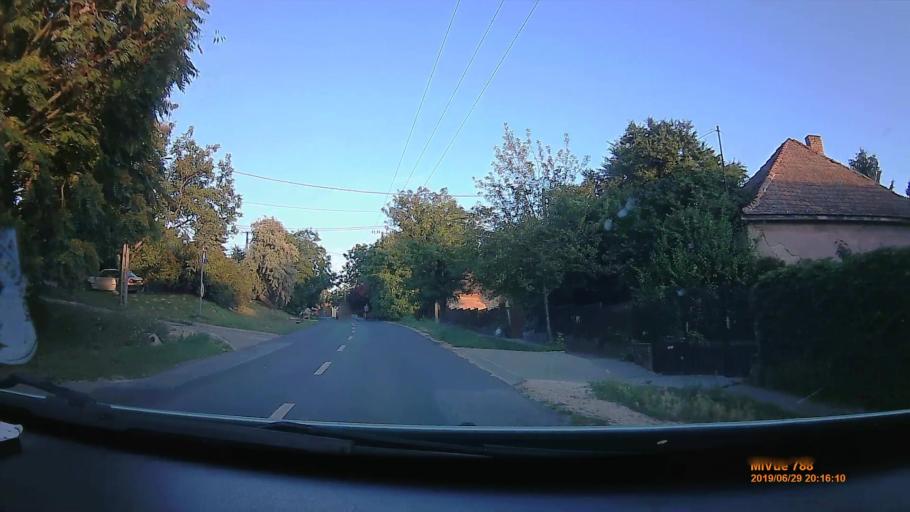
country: HU
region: Pest
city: Paty
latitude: 47.5145
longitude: 18.8354
